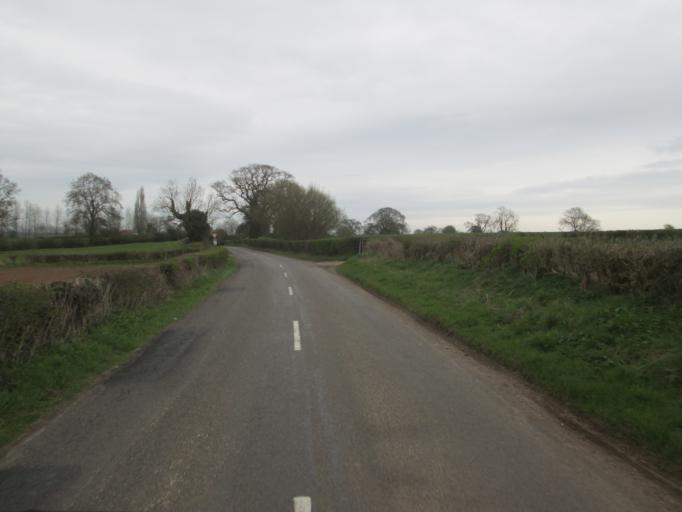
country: GB
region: England
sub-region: Derbyshire
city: Findern
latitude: 52.9373
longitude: -1.5460
